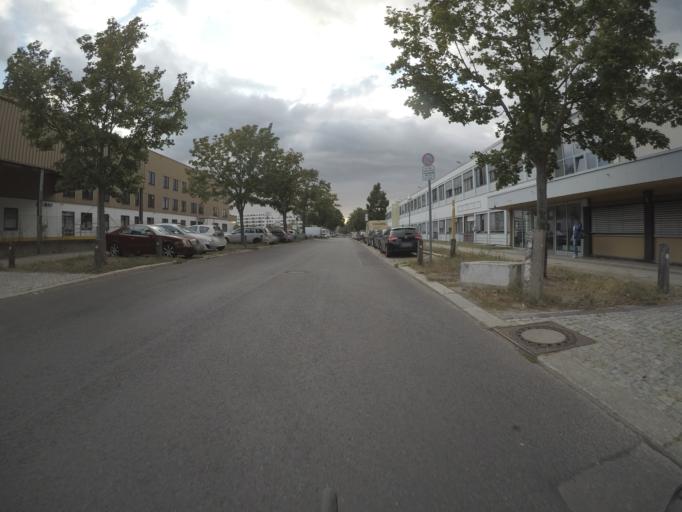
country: DE
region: Berlin
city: Hakenfelde
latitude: 52.5643
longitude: 13.2189
